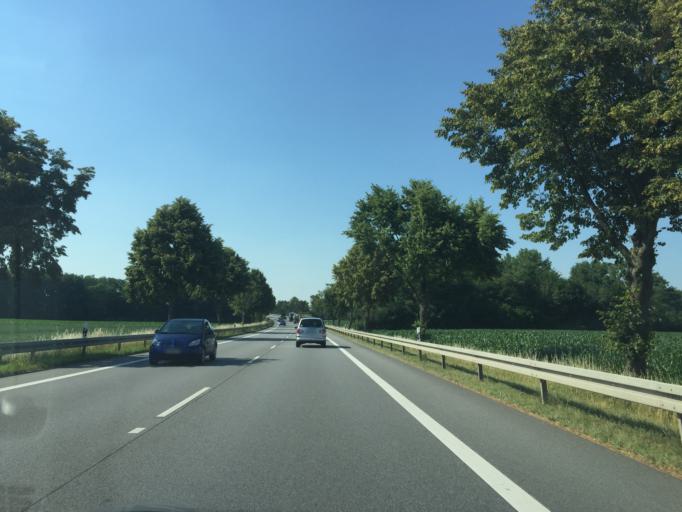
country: DE
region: Hesse
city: Lorsch
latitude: 49.6565
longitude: 8.5809
